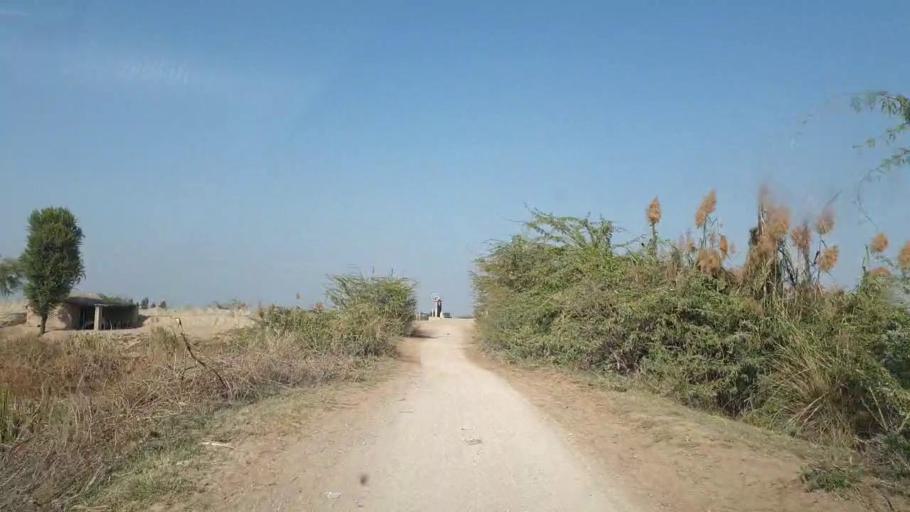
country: PK
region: Sindh
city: Tando Mittha Khan
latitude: 25.7725
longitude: 69.1939
